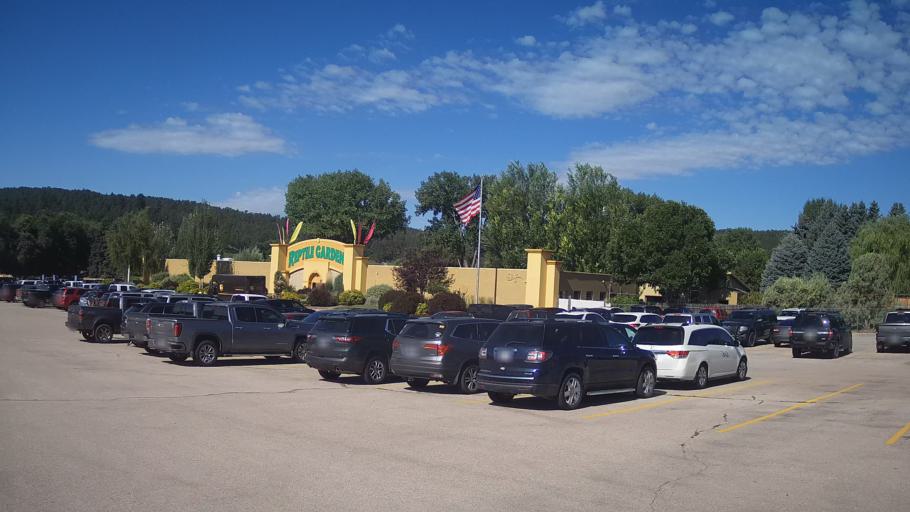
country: US
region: South Dakota
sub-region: Pennington County
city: Colonial Pine Hills
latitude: 43.9910
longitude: -103.2702
